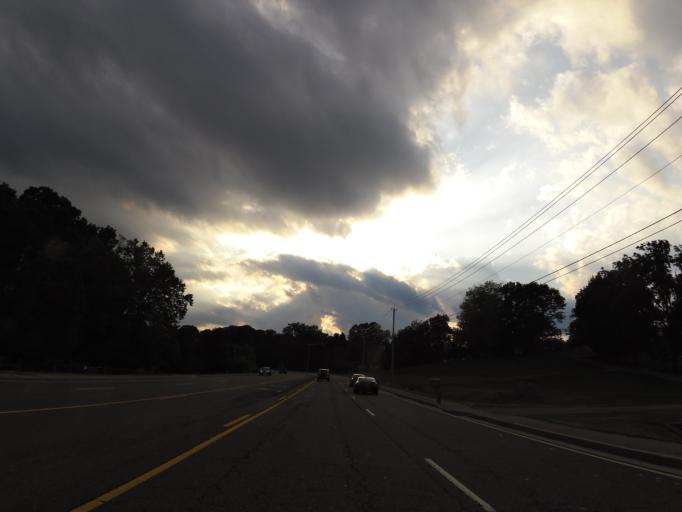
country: US
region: Tennessee
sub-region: Knox County
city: Knoxville
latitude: 36.0733
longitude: -83.9585
